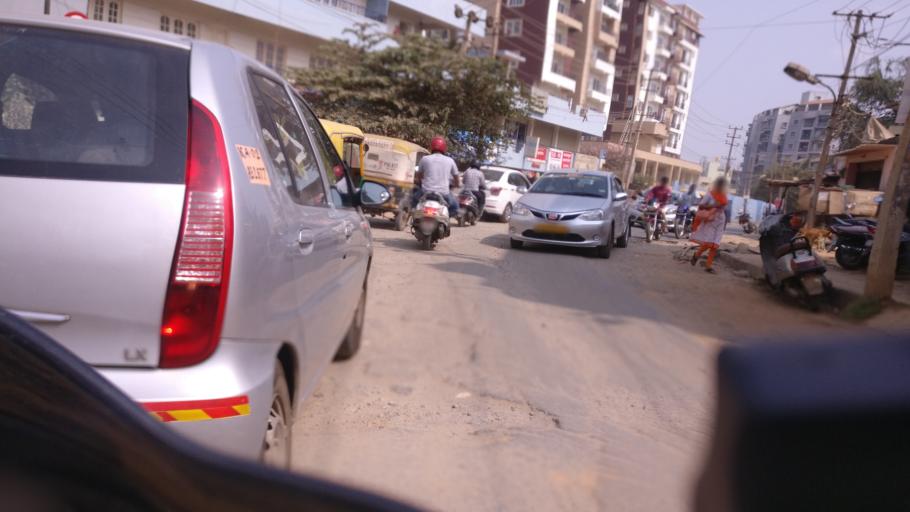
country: IN
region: Karnataka
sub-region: Bangalore Urban
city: Bangalore
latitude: 12.9091
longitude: 77.6761
